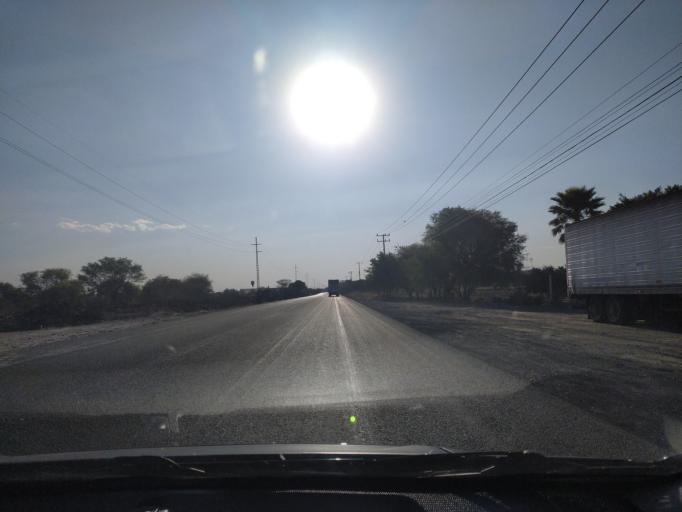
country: MX
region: Michoacan
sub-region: Vista Hermosa
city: Los Pilares
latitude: 20.2744
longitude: -102.4051
